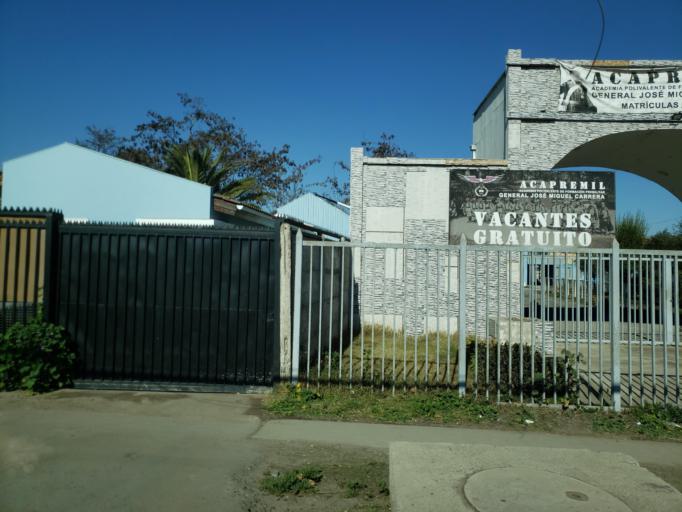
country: CL
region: Santiago Metropolitan
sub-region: Provincia de Talagante
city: El Monte
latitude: -33.6863
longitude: -71.0183
